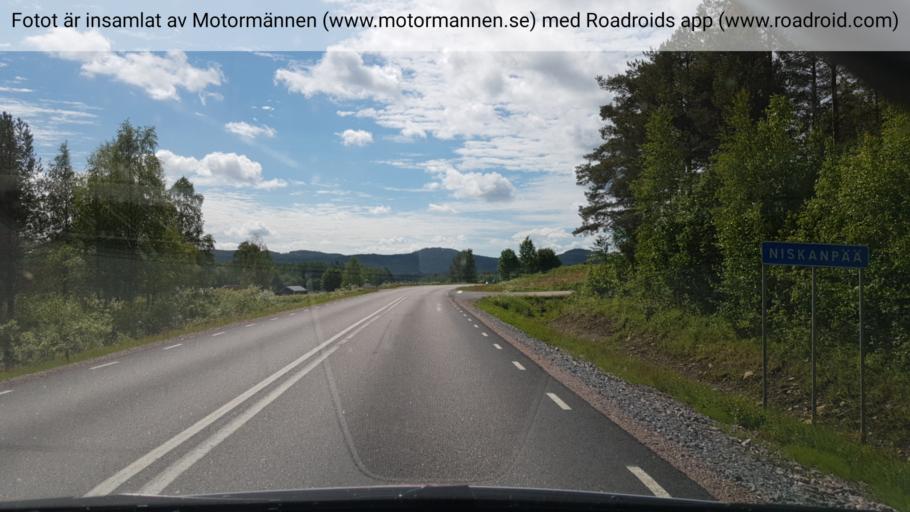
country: SE
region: Norrbotten
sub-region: Overtornea Kommun
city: OEvertornea
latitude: 66.5389
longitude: 23.7832
